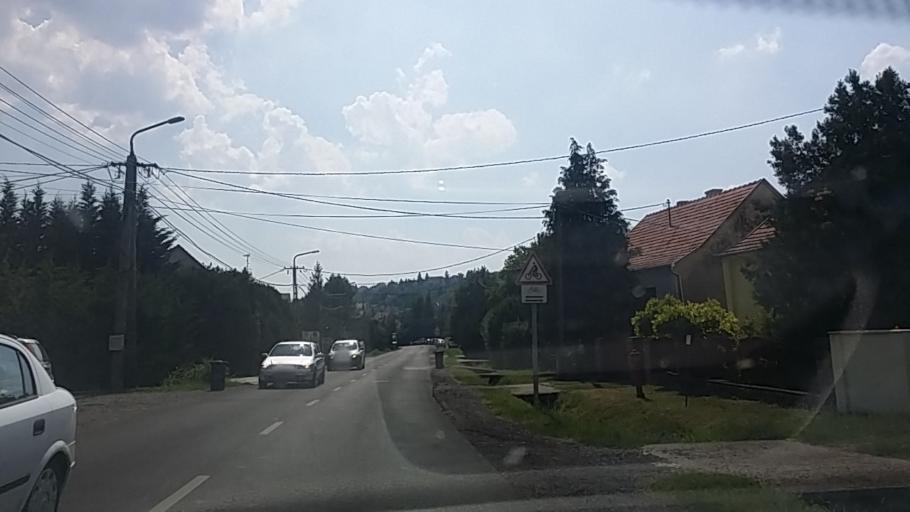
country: HU
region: Baranya
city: Pecs
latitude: 46.0784
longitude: 18.1893
